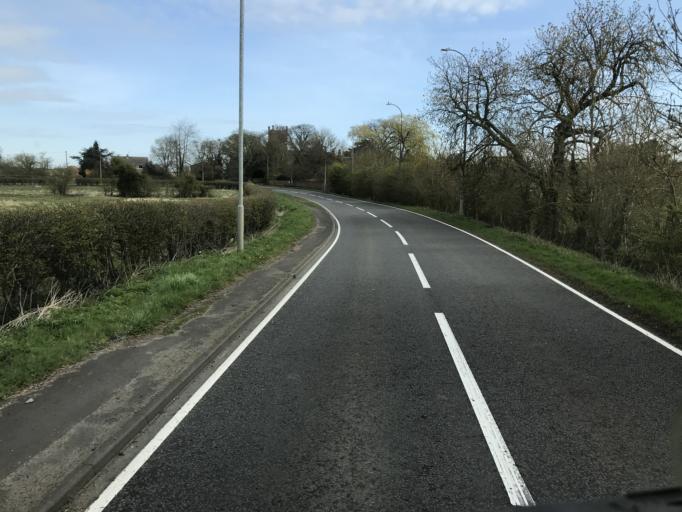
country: GB
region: England
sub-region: Lincolnshire
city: Market Rasen
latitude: 53.3880
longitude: -0.4009
